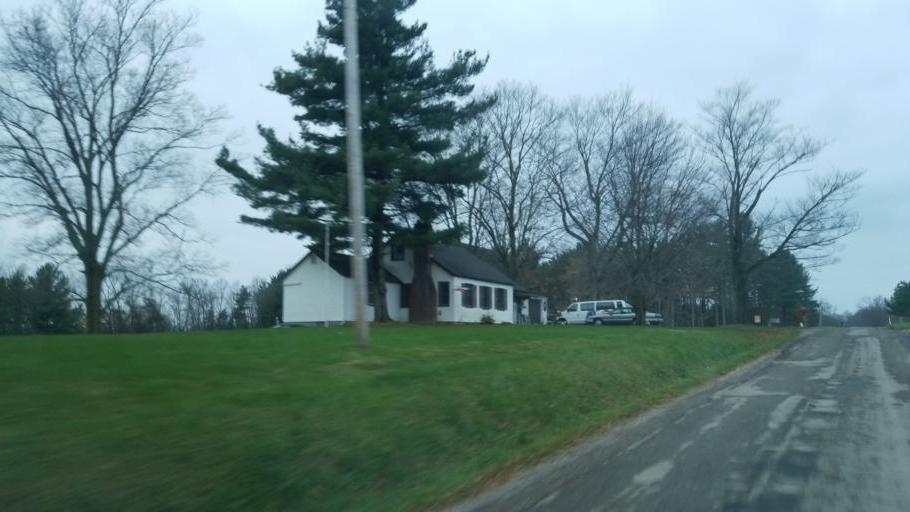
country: US
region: Ohio
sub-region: Knox County
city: Mount Vernon
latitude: 40.3709
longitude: -82.5554
